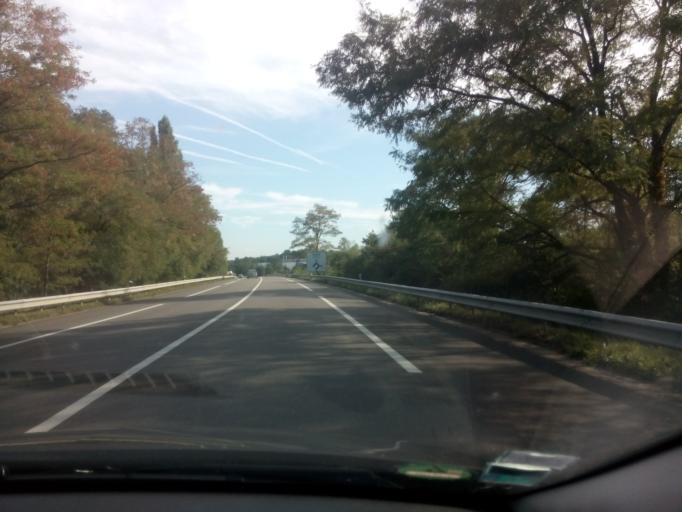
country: FR
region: Alsace
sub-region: Departement du Bas-Rhin
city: Wissembourg
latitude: 49.0251
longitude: 7.9639
